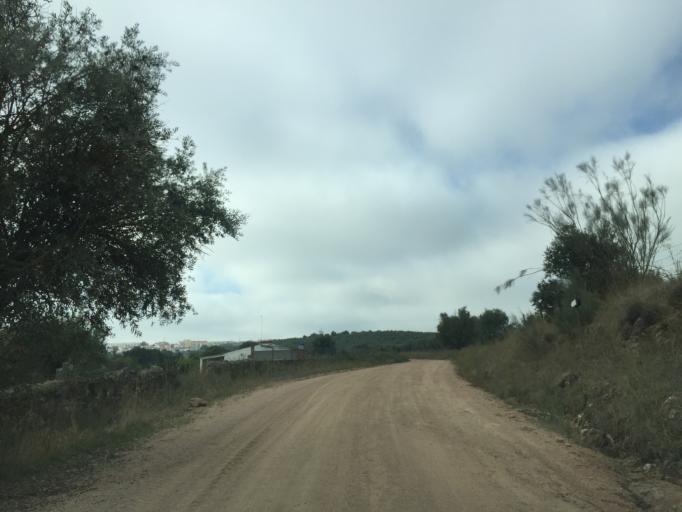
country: PT
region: Portalegre
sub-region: Fronteira
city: Fronteira
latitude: 39.0560
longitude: -7.6348
